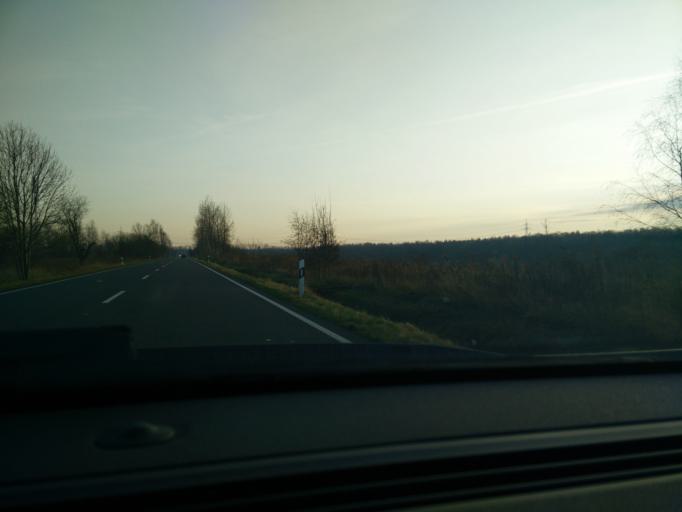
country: DE
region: Saxony
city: Espenhain
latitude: 51.2095
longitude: 12.4511
